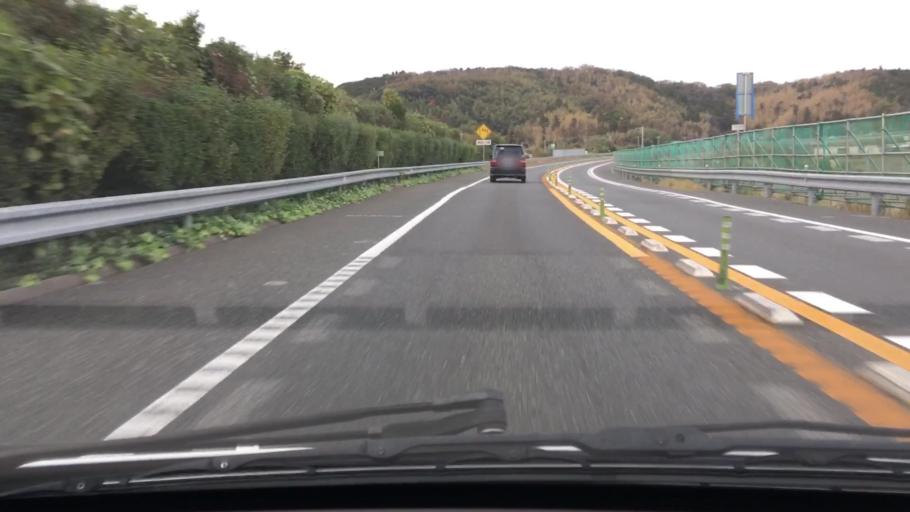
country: JP
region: Chiba
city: Kimitsu
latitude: 35.2204
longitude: 139.8849
